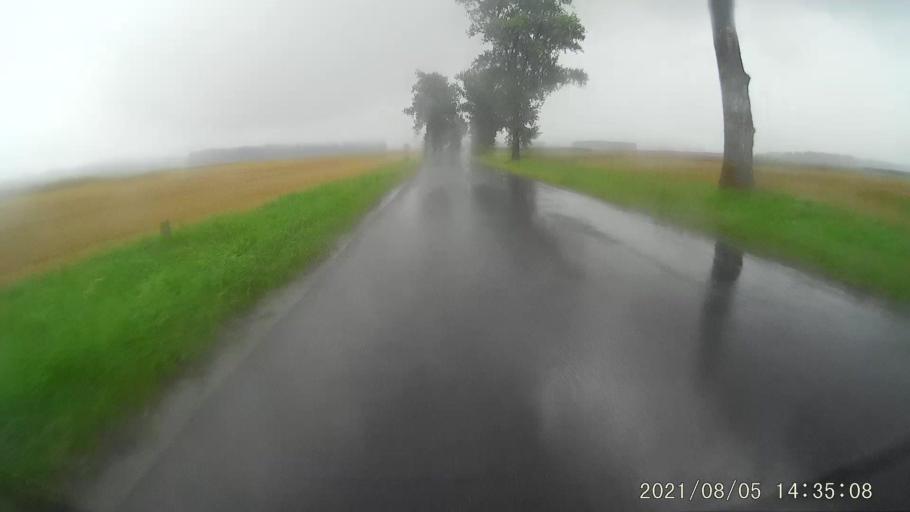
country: PL
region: Opole Voivodeship
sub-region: Powiat nyski
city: Lambinowice
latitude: 50.4674
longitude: 17.5070
